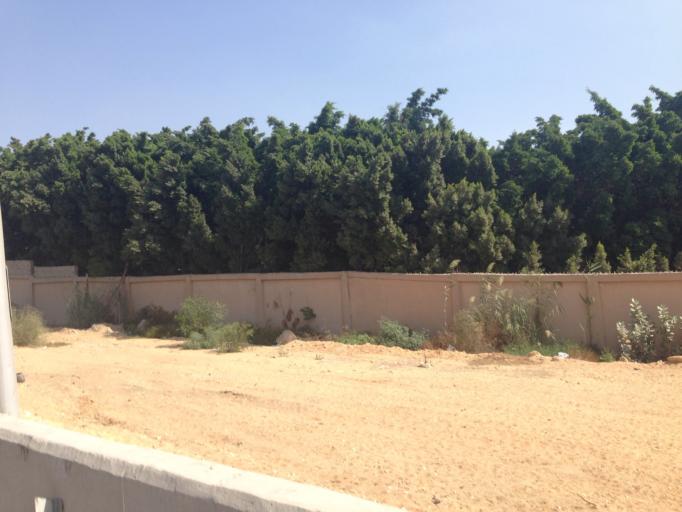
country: EG
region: Muhafazat al Qalyubiyah
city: Al Khankah
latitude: 30.0701
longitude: 31.4285
